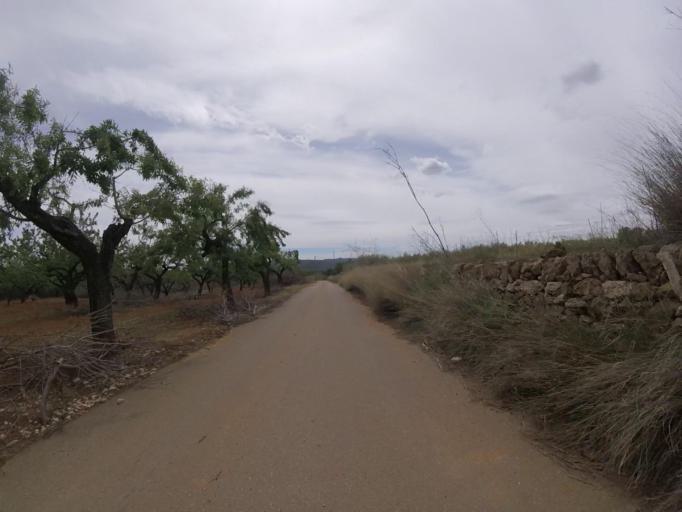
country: ES
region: Valencia
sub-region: Provincia de Castello
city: Benlloch
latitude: 40.1761
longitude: -0.0057
